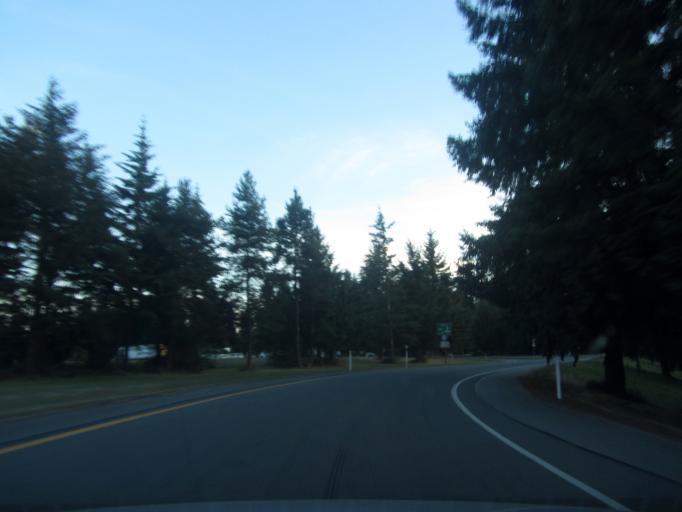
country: US
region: Washington
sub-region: Snohomish County
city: Smokey Point
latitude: 48.1708
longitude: -122.1927
